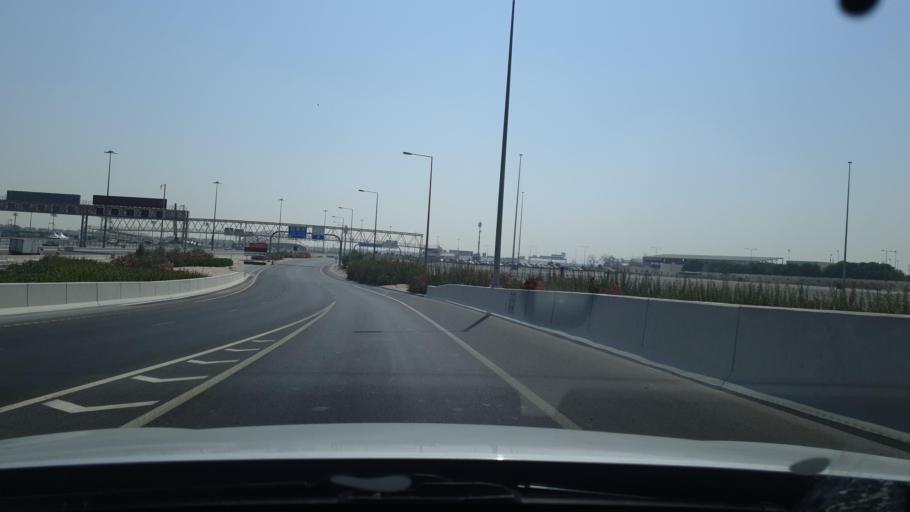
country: QA
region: Baladiyat ad Dawhah
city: Doha
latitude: 25.2331
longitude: 51.5272
